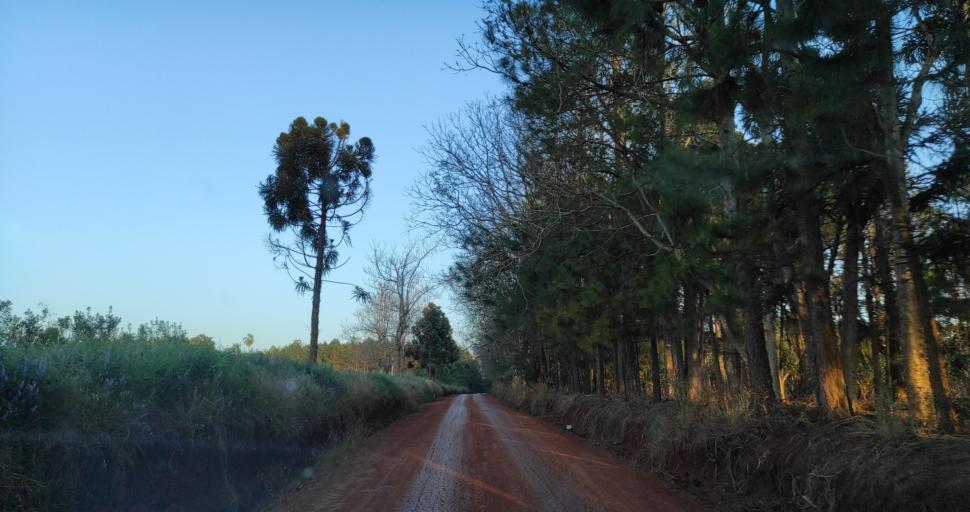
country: AR
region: Misiones
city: Capiovi
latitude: -26.8750
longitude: -55.0962
